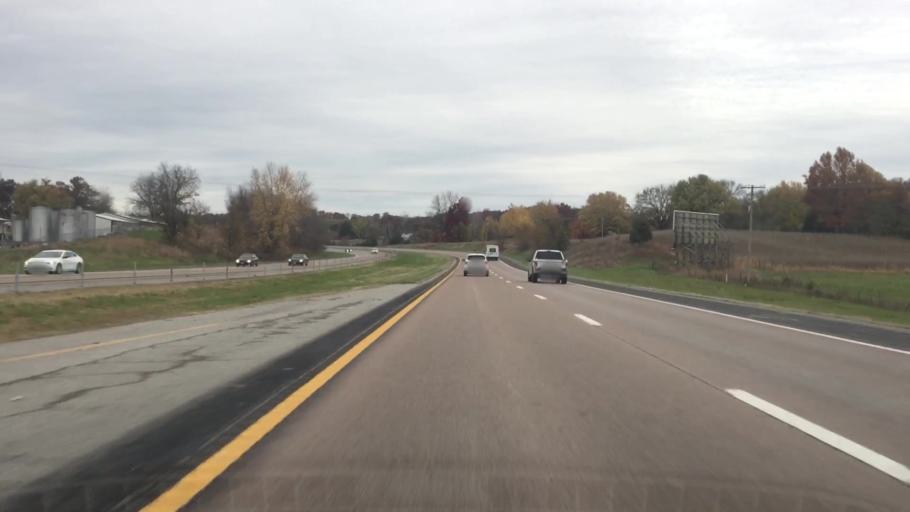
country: US
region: Missouri
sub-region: Cole County
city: Jefferson City
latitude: 38.6474
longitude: -92.2025
